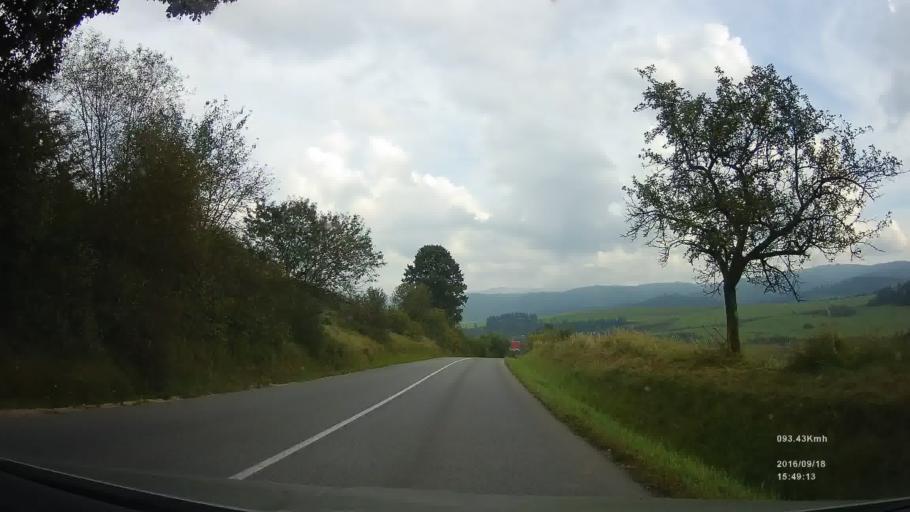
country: SK
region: Kosicky
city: Spisska Nova Ves
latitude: 48.9194
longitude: 20.6060
